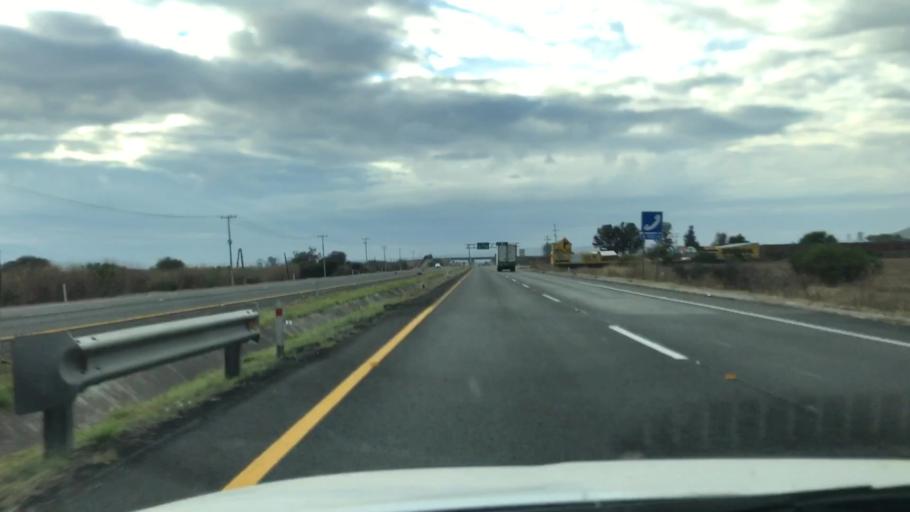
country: MX
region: Guanajuato
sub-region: Penjamo
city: Mezquite de Luna
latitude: 20.3787
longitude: -101.8561
